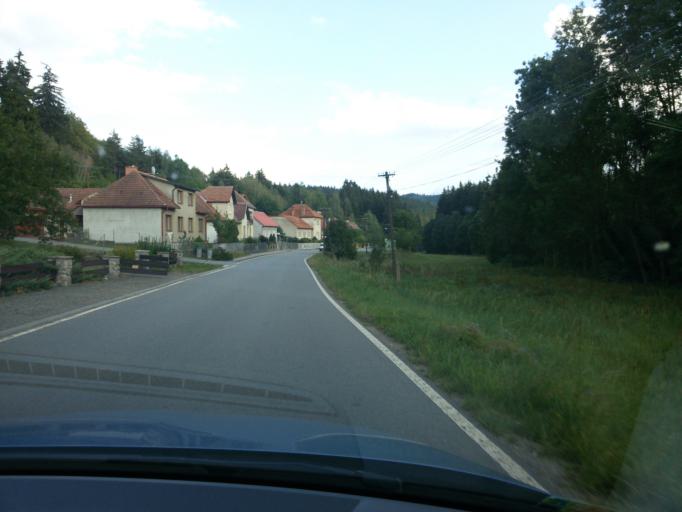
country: CZ
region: South Moravian
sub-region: Okres Brno-Venkov
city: Lomnice
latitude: 49.4591
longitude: 16.4303
